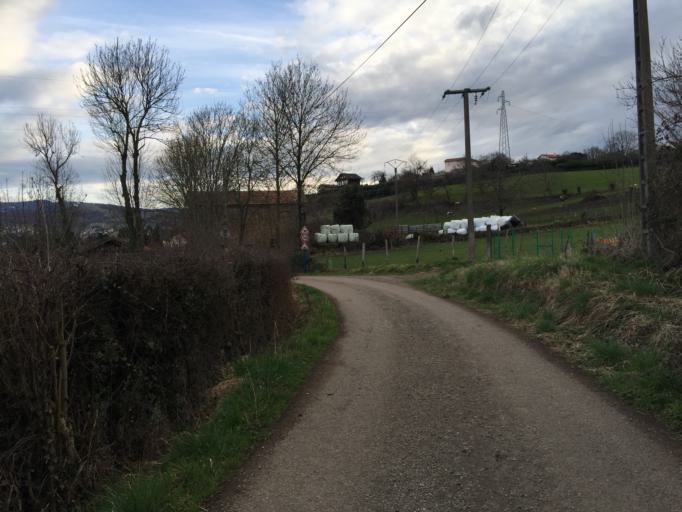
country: FR
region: Rhone-Alpes
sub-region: Departement de la Loire
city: Saint-Chamond
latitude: 45.4853
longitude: 4.5081
